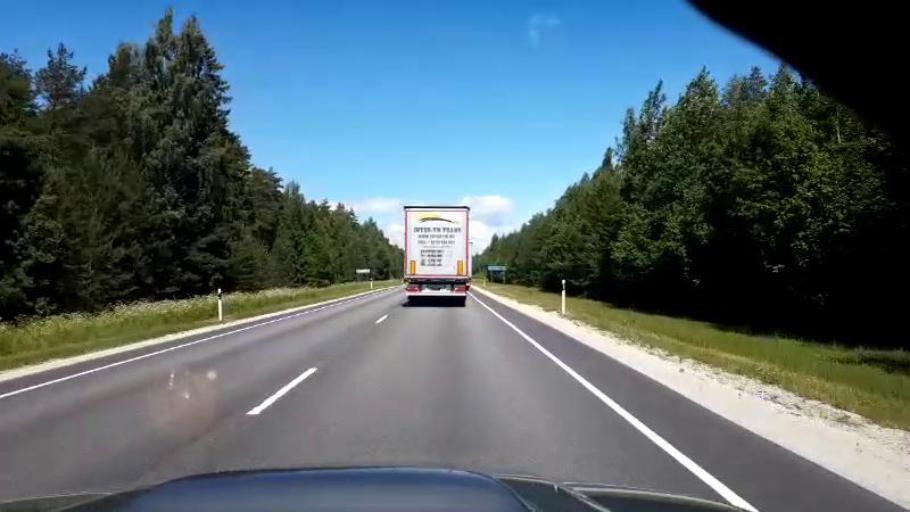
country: EE
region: Paernumaa
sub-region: Paernu linn
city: Parnu
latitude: 58.1121
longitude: 24.5096
